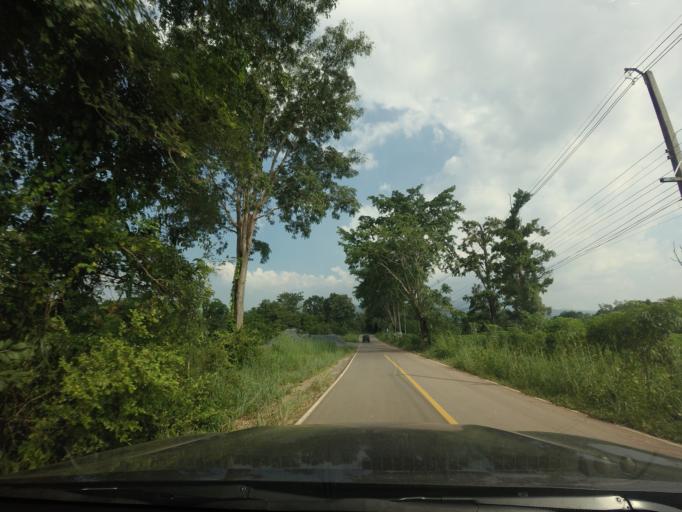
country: TH
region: Phitsanulok
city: Nakhon Thai
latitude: 17.0437
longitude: 100.9117
